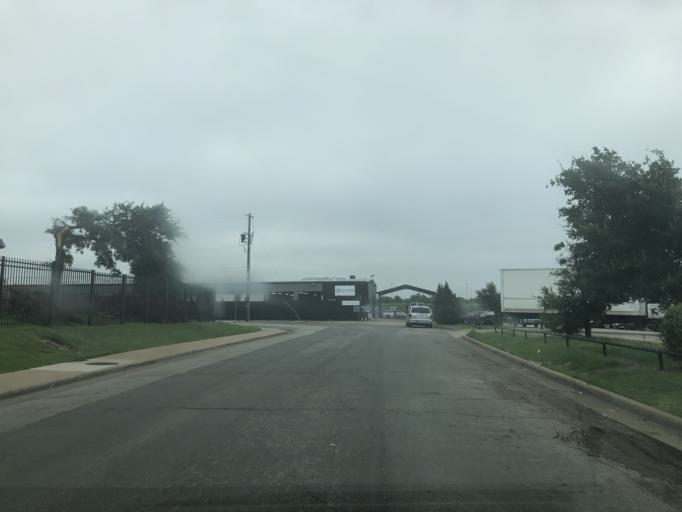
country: US
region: Texas
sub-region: Dallas County
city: University Park
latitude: 32.8595
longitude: -96.8632
